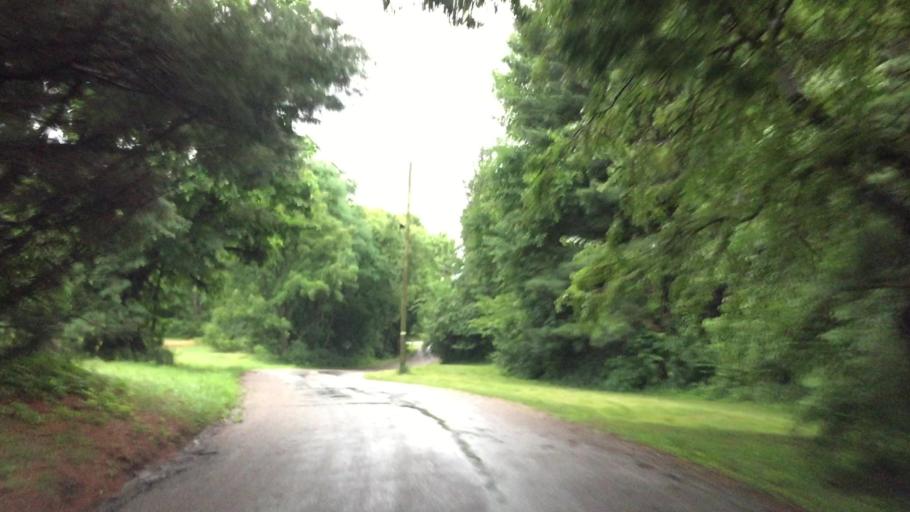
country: US
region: Illinois
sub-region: Hancock County
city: Nauvoo
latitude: 40.5396
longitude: -91.3760
